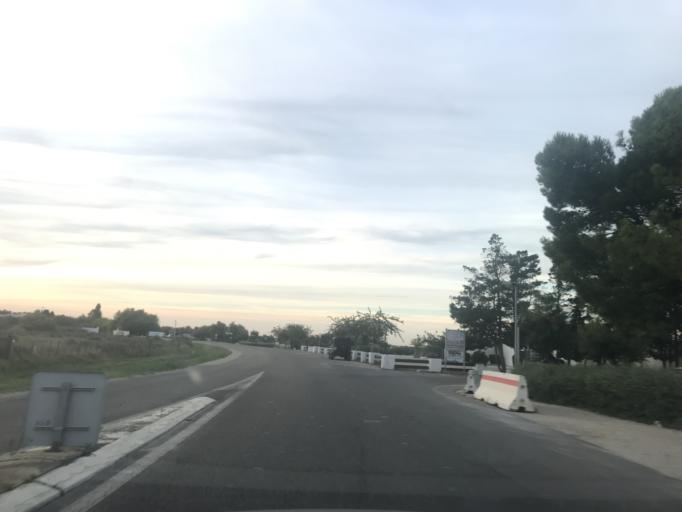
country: FR
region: Provence-Alpes-Cote d'Azur
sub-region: Departement des Bouches-du-Rhone
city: Saintes-Maries-de-la-Mer
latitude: 43.4570
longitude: 4.4268
